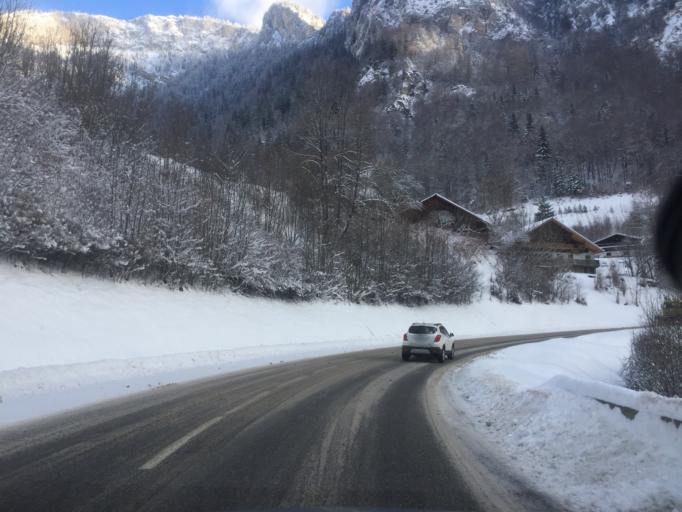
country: FR
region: Rhone-Alpes
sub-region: Departement de la Haute-Savoie
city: Abondance
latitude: 46.2879
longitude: 6.6928
